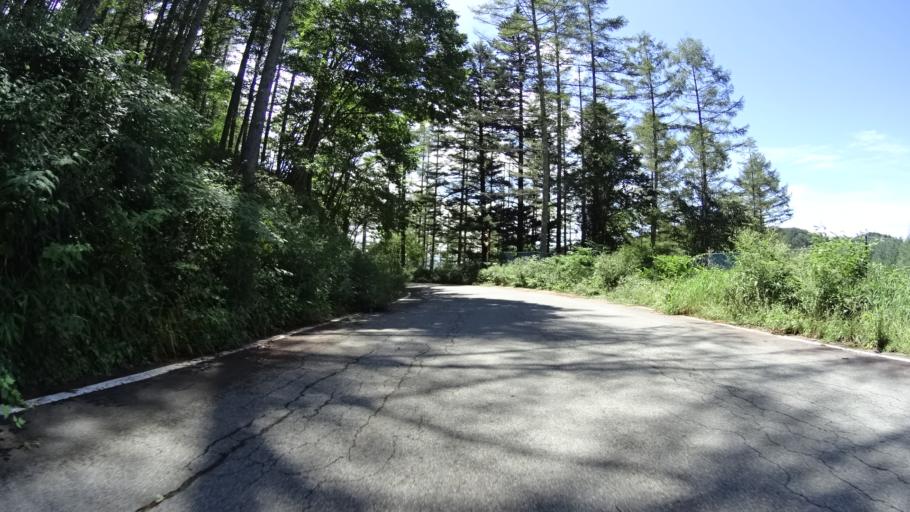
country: JP
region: Yamanashi
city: Enzan
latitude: 35.7283
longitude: 138.8433
